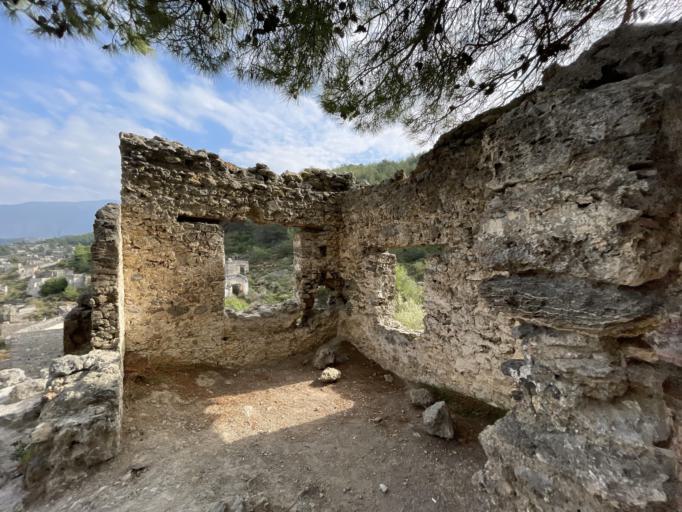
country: TR
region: Mugla
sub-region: Fethiye
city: Fethiye
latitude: 36.5730
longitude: 29.0861
